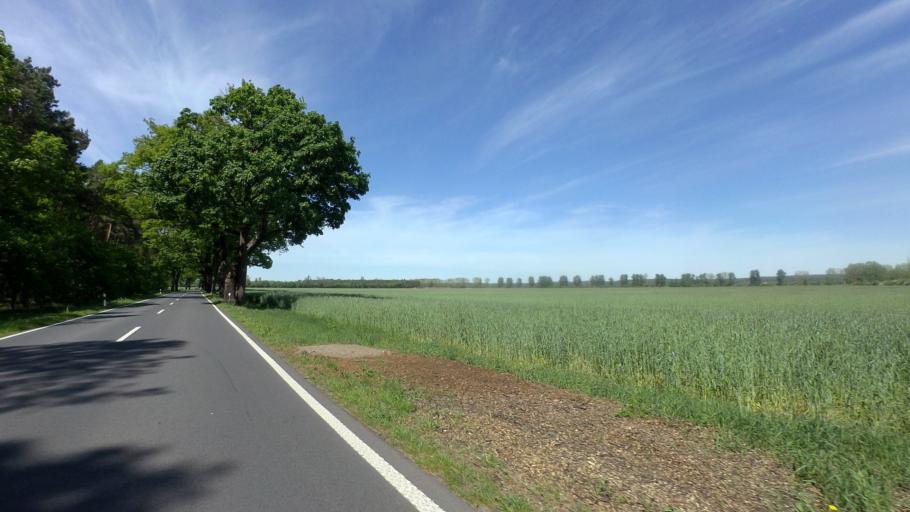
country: DE
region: Brandenburg
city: Baruth
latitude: 52.0685
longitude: 13.4676
